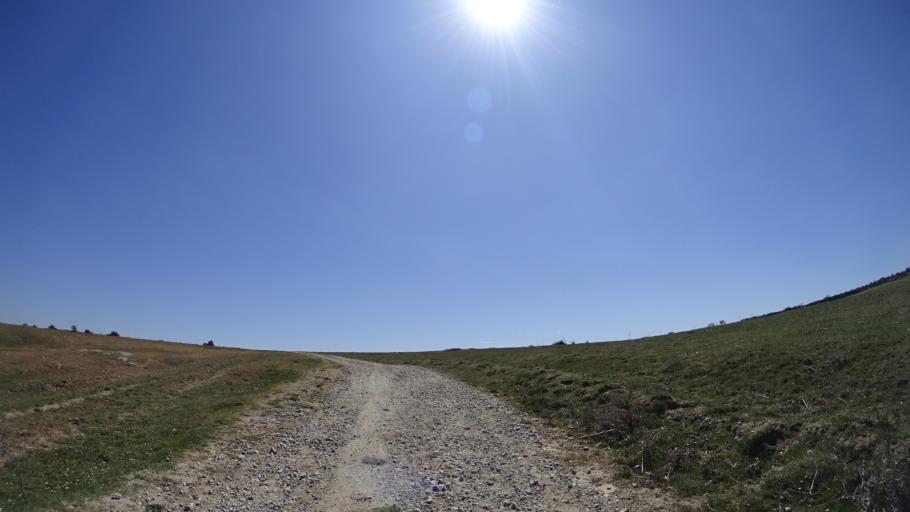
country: ES
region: Madrid
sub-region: Provincia de Madrid
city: Colmenar Viejo
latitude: 40.6919
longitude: -3.7565
